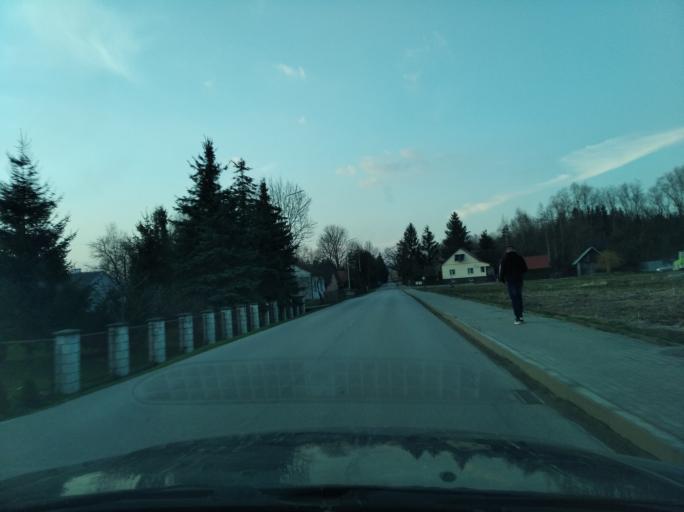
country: PL
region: Subcarpathian Voivodeship
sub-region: Powiat przeworski
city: Zurawiczki
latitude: 50.0299
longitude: 22.5132
